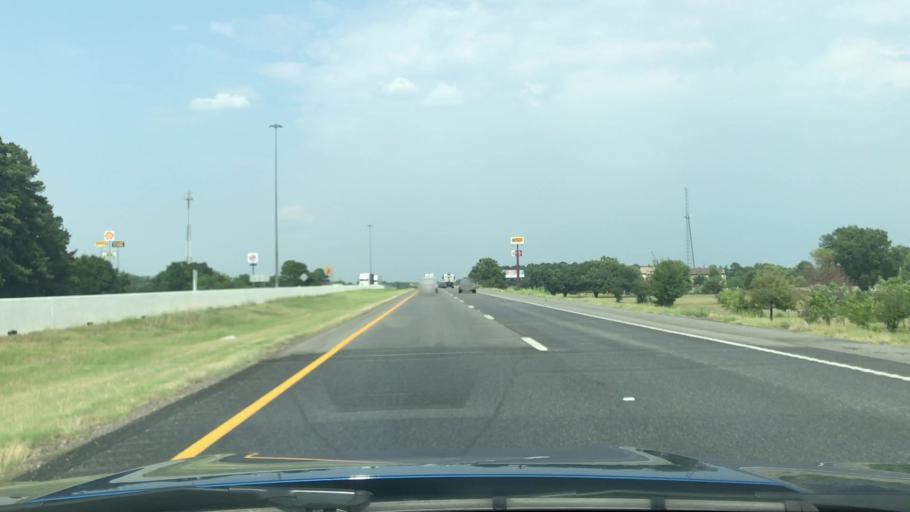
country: US
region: Texas
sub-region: Gregg County
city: Longview
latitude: 32.4490
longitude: -94.7118
